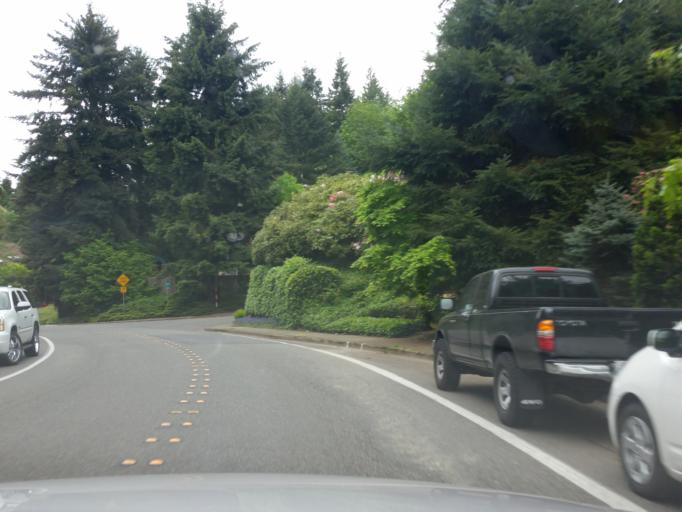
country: US
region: Washington
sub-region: King County
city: Yarrow Point
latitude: 47.6448
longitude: -122.1921
